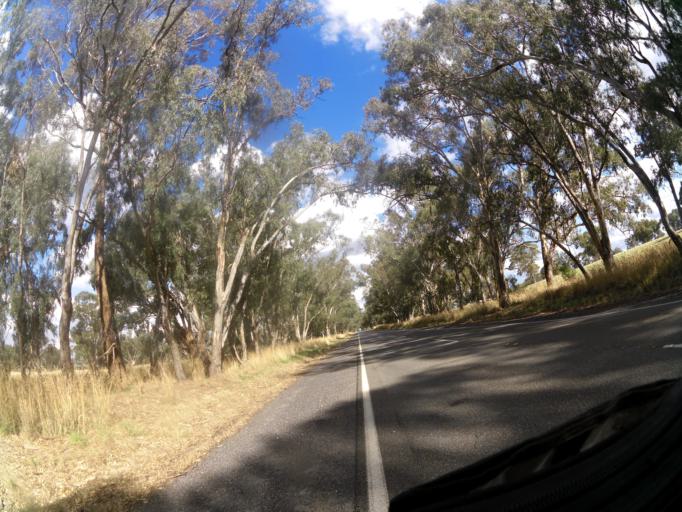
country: AU
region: Victoria
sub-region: Mansfield
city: Mansfield
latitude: -37.0092
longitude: 146.0833
